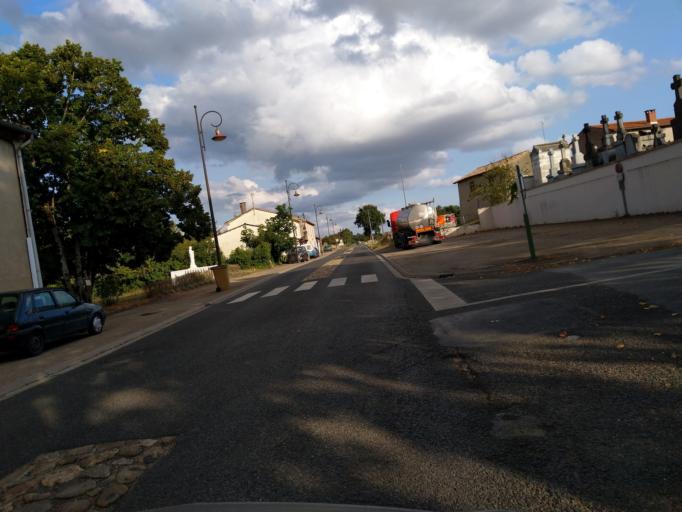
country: FR
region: Midi-Pyrenees
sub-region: Departement du Tarn
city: Frejairolles
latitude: 43.8799
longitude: 2.2316
